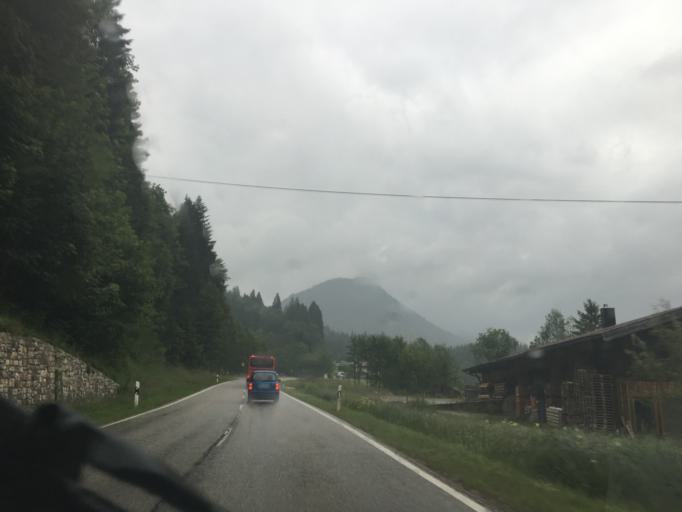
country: DE
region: Bavaria
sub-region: Upper Bavaria
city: Reit im Winkl
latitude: 47.6900
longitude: 12.4942
